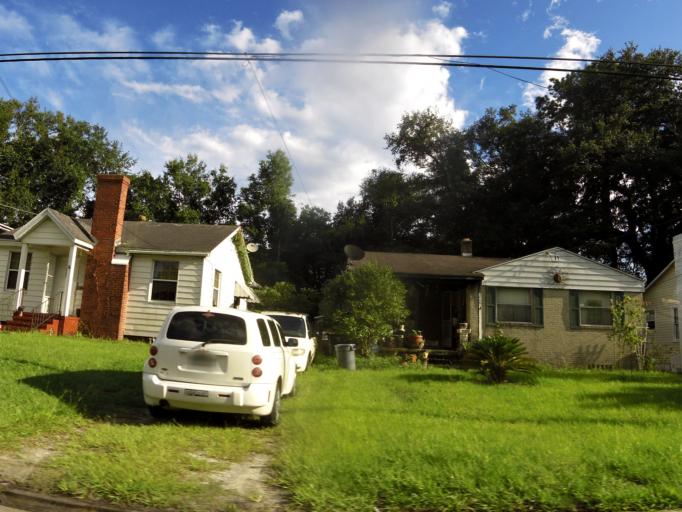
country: US
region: Florida
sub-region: Duval County
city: Jacksonville
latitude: 30.3140
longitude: -81.7068
